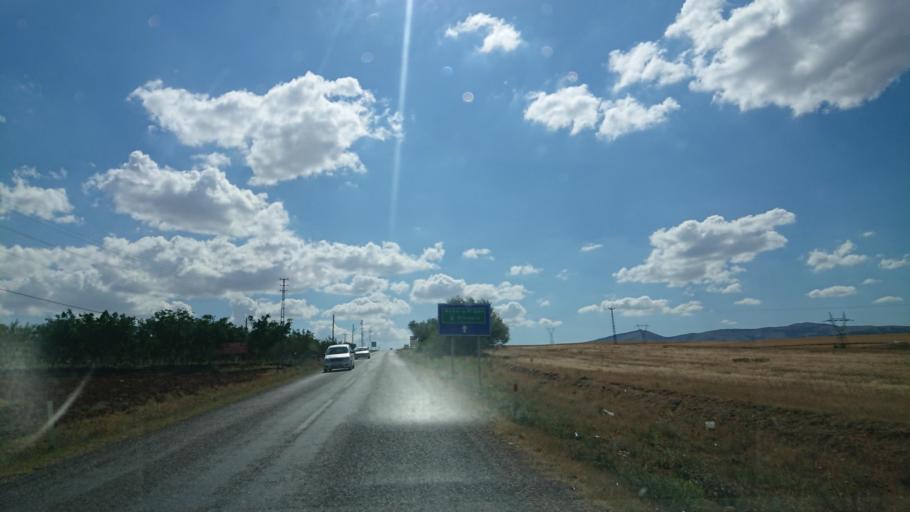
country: TR
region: Kirsehir
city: Kirsehir
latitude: 39.1534
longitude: 34.1140
